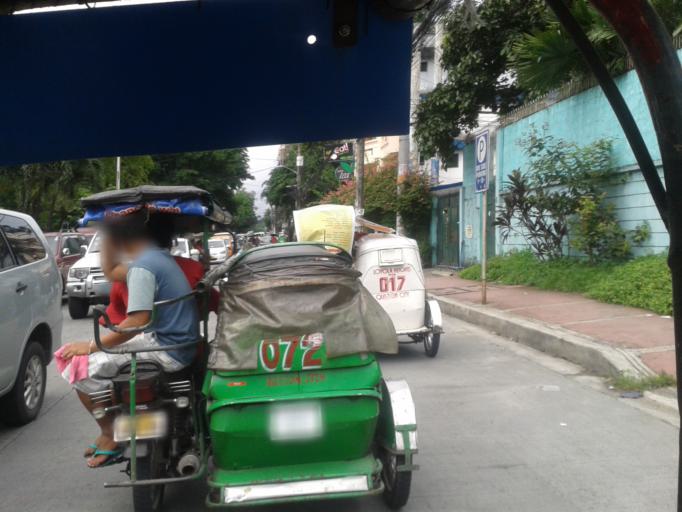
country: PH
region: Metro Manila
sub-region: Marikina
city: Calumpang
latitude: 14.6379
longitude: 121.0732
